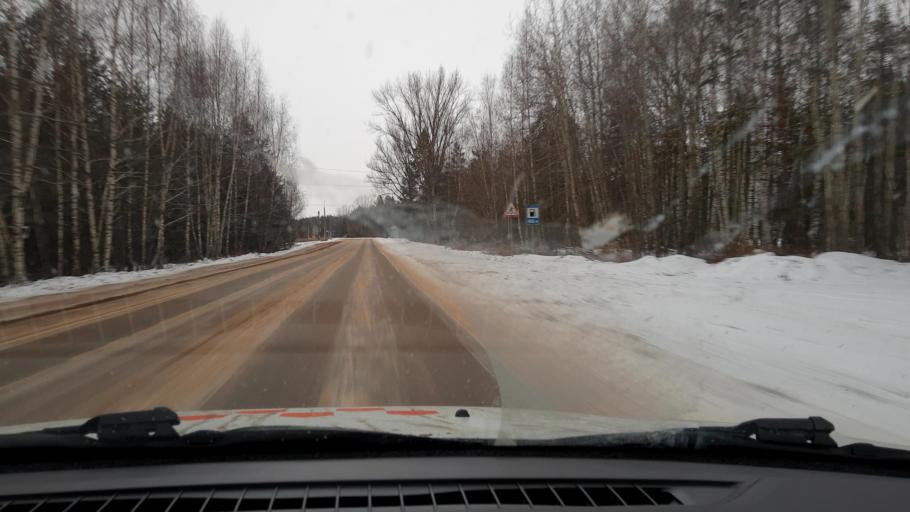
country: RU
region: Nizjnij Novgorod
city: Afonino
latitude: 56.3228
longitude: 44.1472
